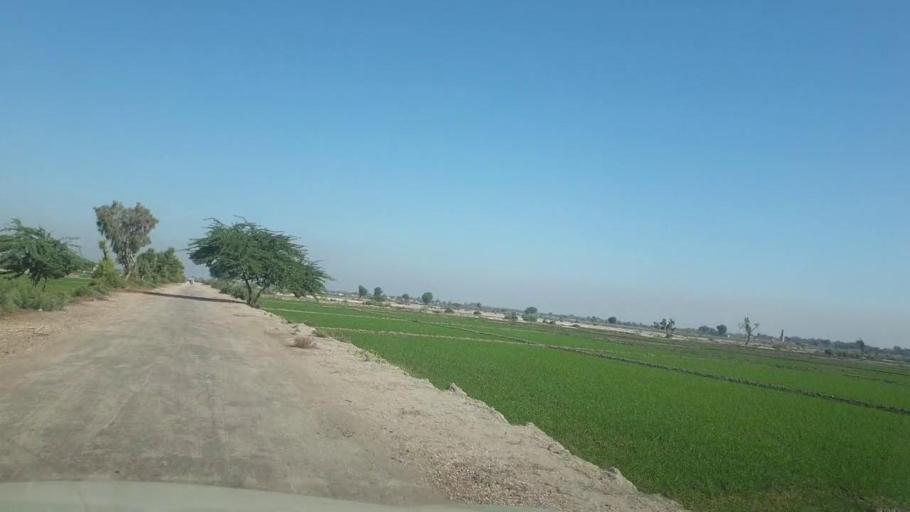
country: PK
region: Sindh
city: Bhan
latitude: 26.5366
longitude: 67.6454
